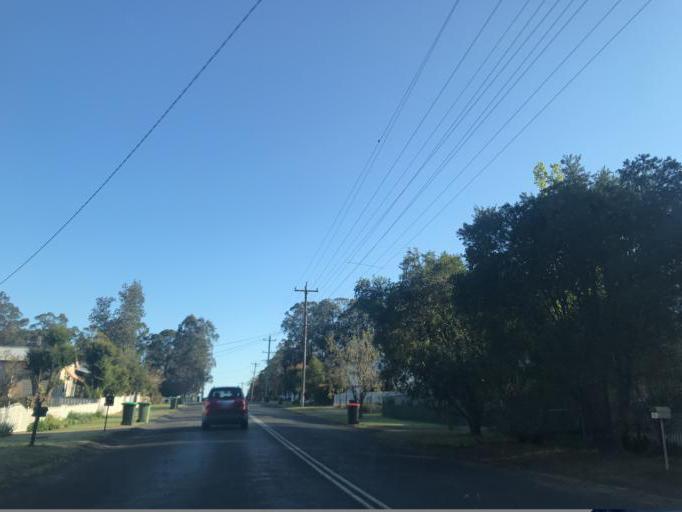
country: AU
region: New South Wales
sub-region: Cessnock
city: Cessnock
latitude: -32.8785
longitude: 151.3116
